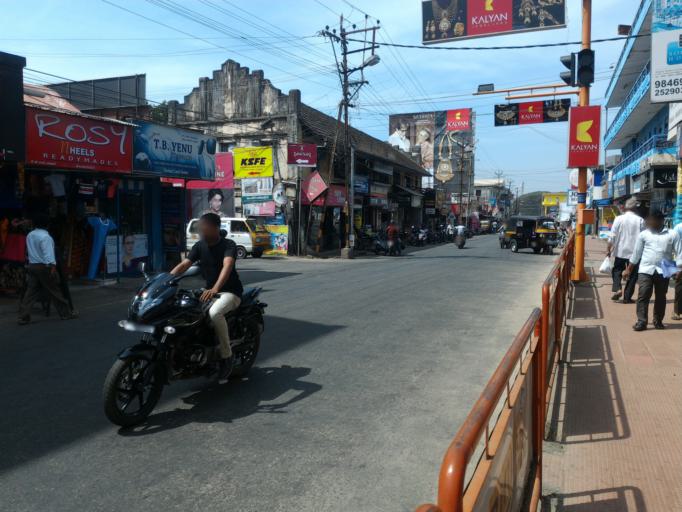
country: IN
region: Kerala
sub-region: Palakkad district
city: Palakkad
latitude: 10.7733
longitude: 76.6569
